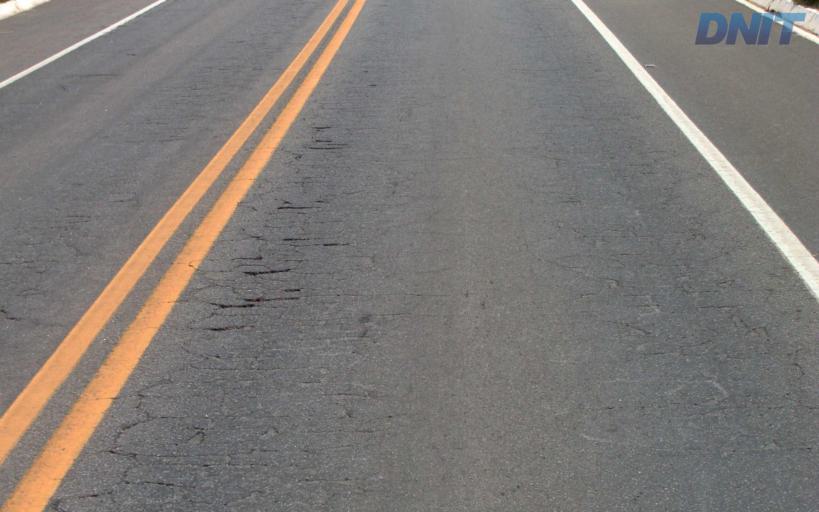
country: BR
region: Minas Gerais
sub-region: Governador Valadares
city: Governador Valadares
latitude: -18.8819
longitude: -41.9950
